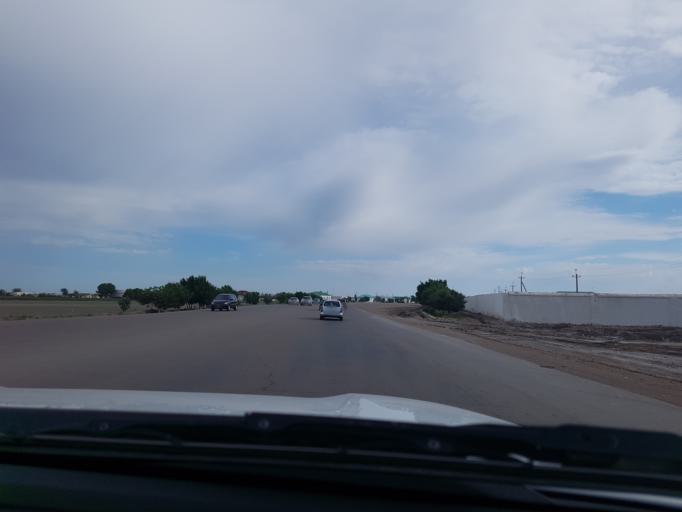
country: TM
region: Dasoguz
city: Dasoguz
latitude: 41.9066
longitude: 59.9354
